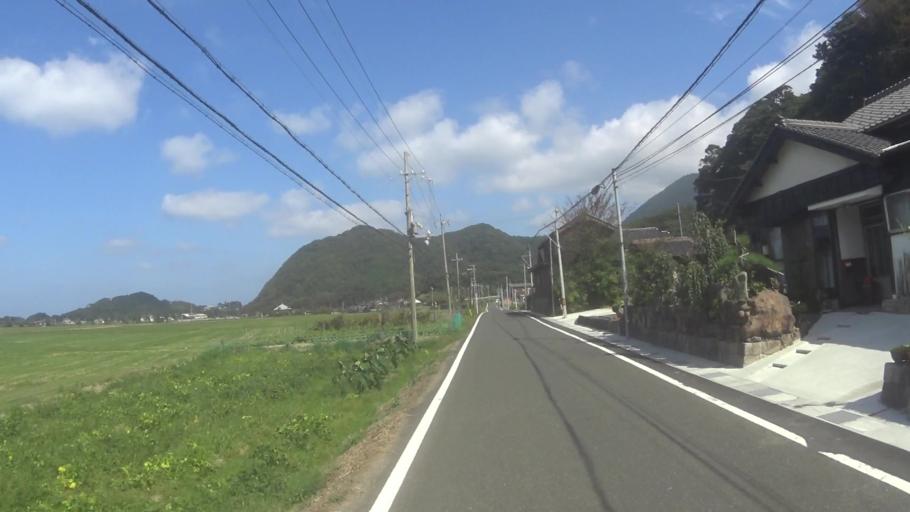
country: JP
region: Kyoto
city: Miyazu
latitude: 35.7316
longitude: 135.1057
